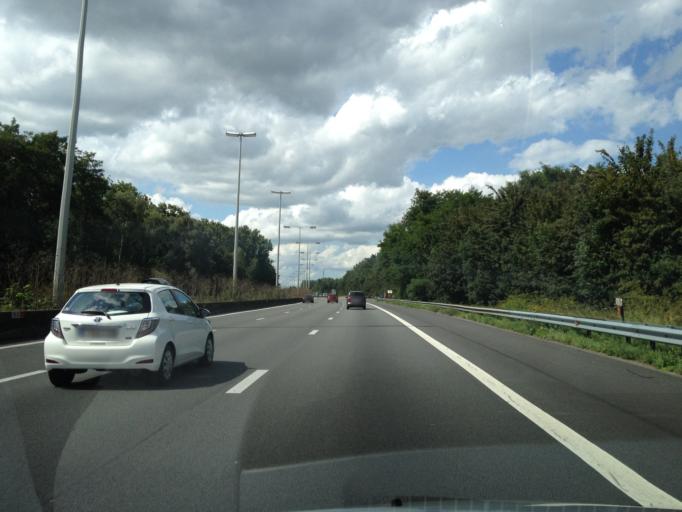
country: BE
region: Flanders
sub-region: Provincie Oost-Vlaanderen
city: Denderleeuw
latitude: 50.9113
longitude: 4.0628
